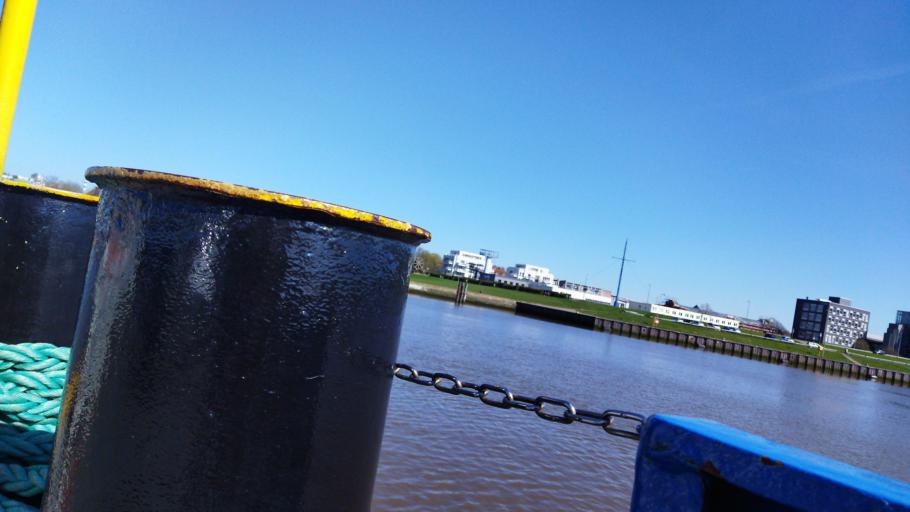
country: DE
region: Bremen
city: Bremerhaven
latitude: 53.5355
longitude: 8.5768
